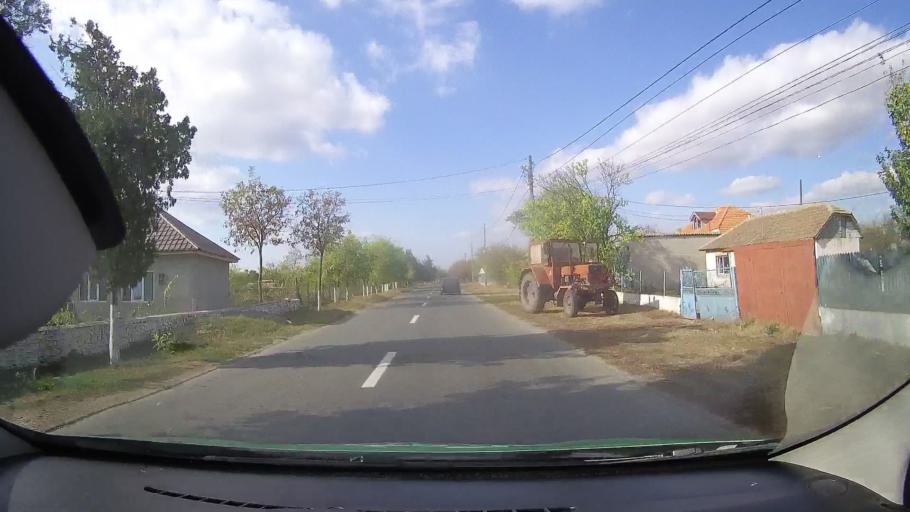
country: RO
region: Constanta
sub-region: Comuna Istria
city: Nuntasi
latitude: 44.5363
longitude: 28.6571
